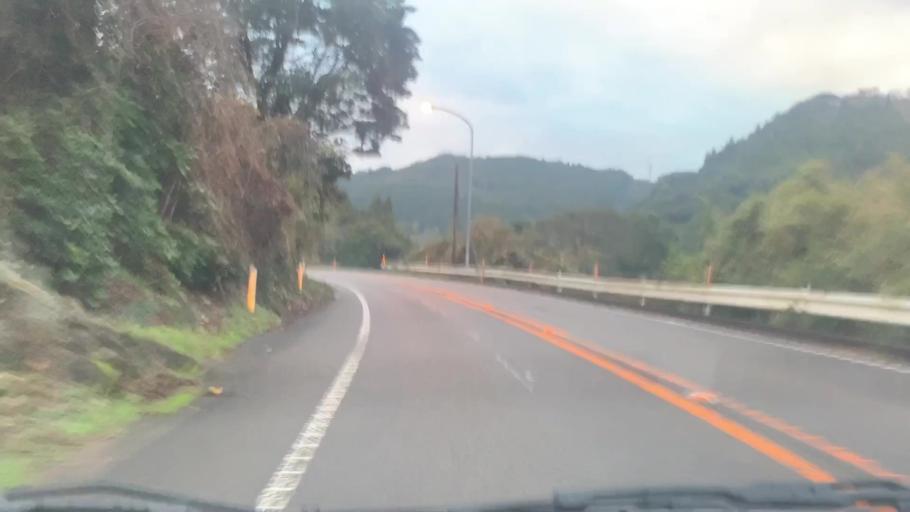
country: JP
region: Saga Prefecture
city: Ureshinomachi-shimojuku
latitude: 33.0709
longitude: 129.9615
